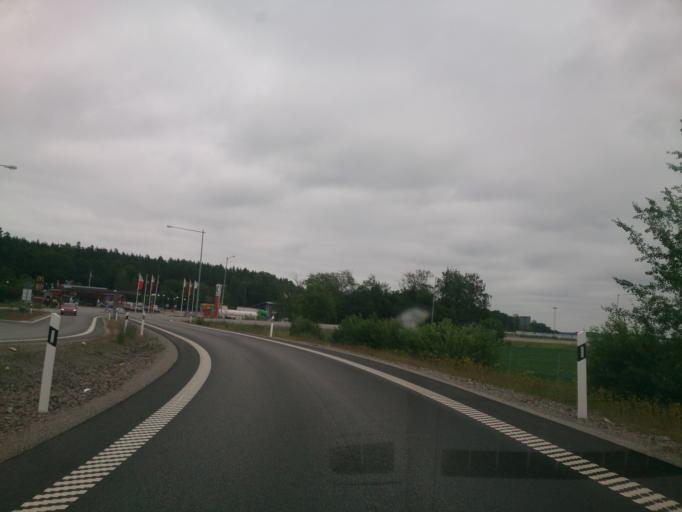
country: SE
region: OEstergoetland
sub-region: Norrkopings Kommun
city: Norrkoping
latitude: 58.5674
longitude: 16.0768
